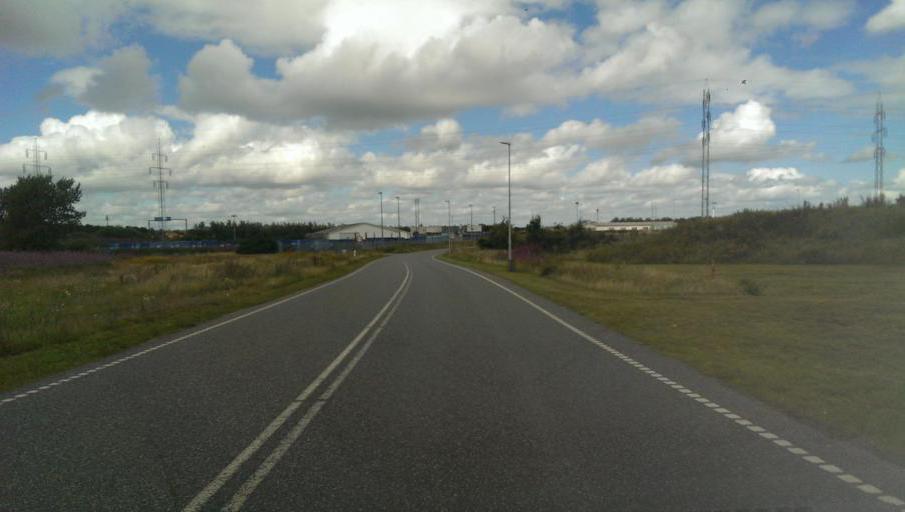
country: DK
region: South Denmark
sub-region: Esbjerg Kommune
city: Esbjerg
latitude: 55.4625
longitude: 8.5067
